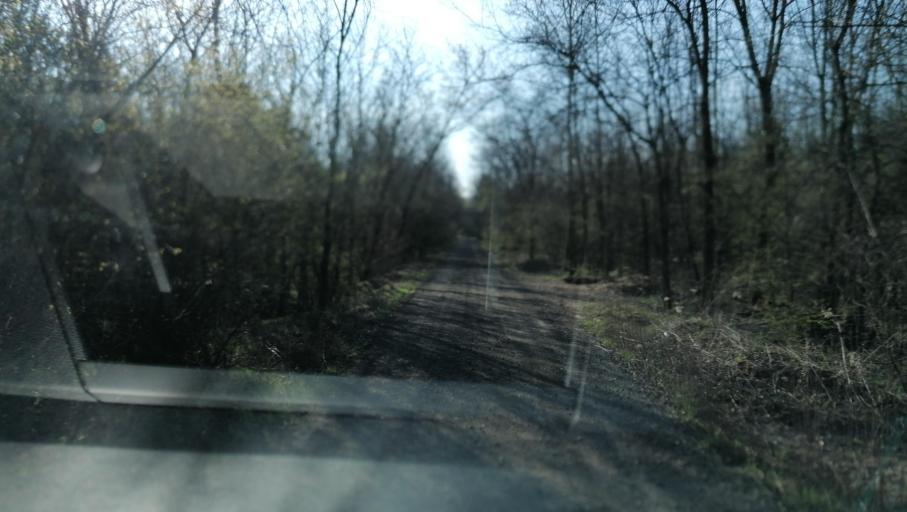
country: HU
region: Pest
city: Szentendre
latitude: 47.6696
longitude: 19.0891
